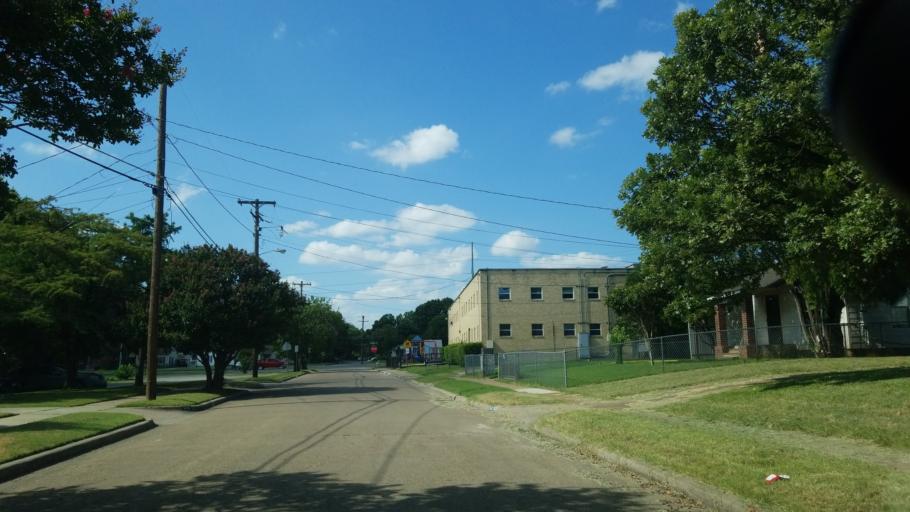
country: US
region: Texas
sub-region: Dallas County
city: Balch Springs
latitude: 32.7727
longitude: -96.7071
